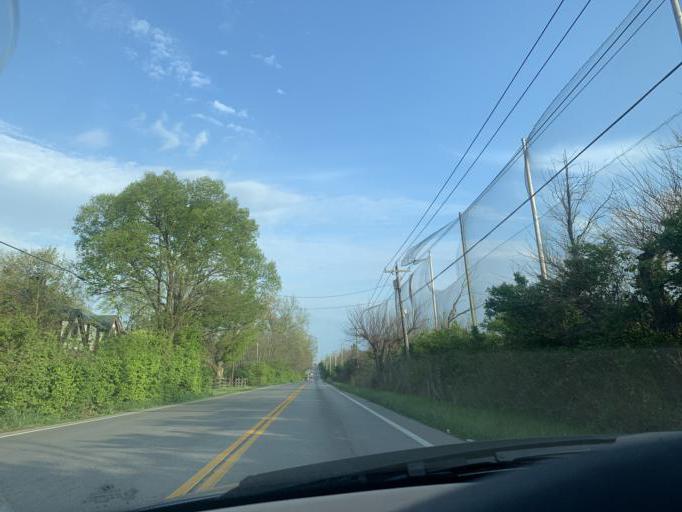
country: US
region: Ohio
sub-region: Hamilton County
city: Springdale
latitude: 39.2734
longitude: -84.4777
